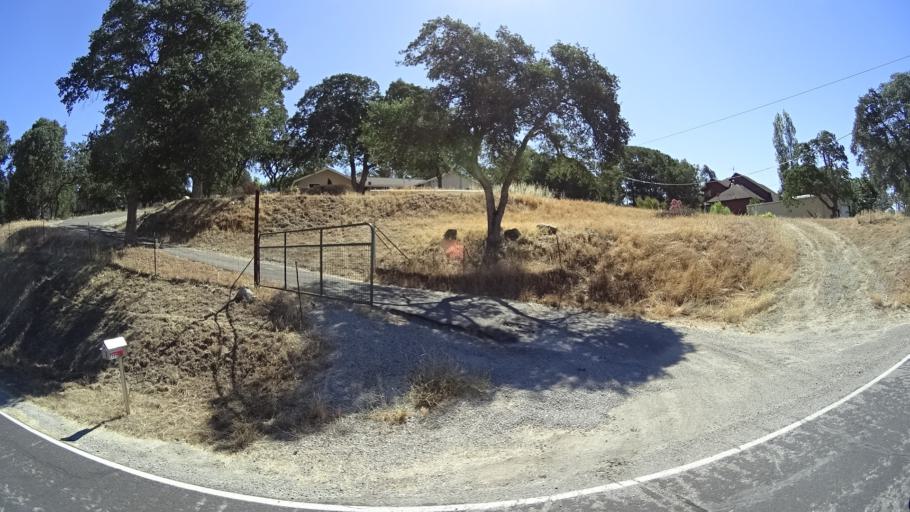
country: US
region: California
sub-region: Calaveras County
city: Rancho Calaveras
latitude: 38.1059
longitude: -120.8757
